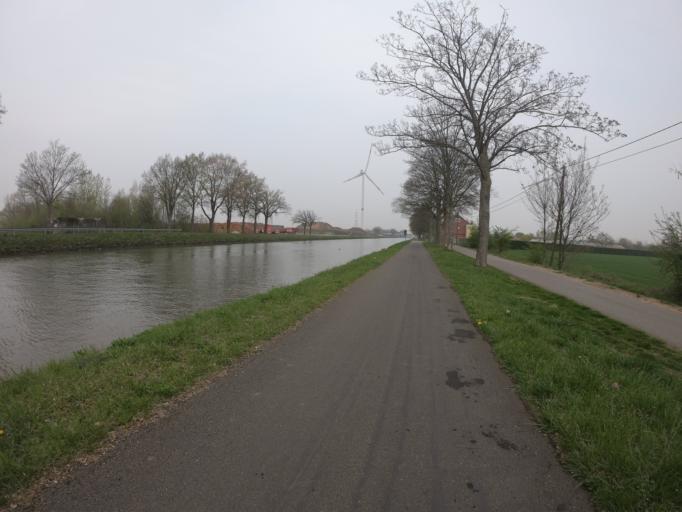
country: BE
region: Flanders
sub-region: Provincie Limburg
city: Maasmechelen
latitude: 50.9453
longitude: 5.7111
